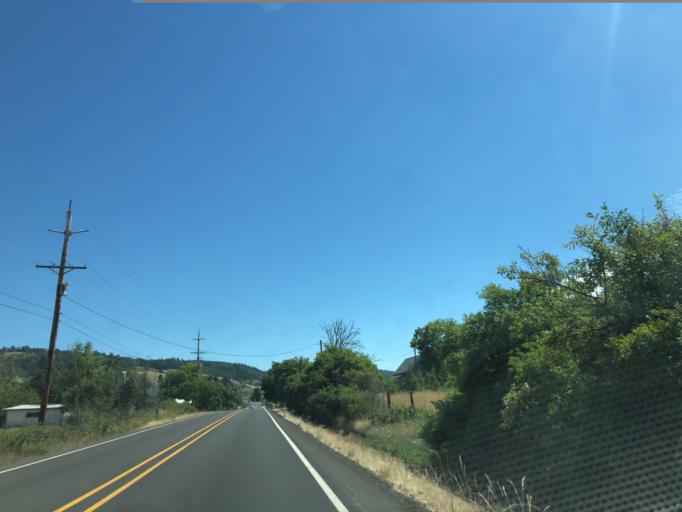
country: US
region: Oregon
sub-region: Douglas County
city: Yoncalla
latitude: 43.5702
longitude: -123.2809
